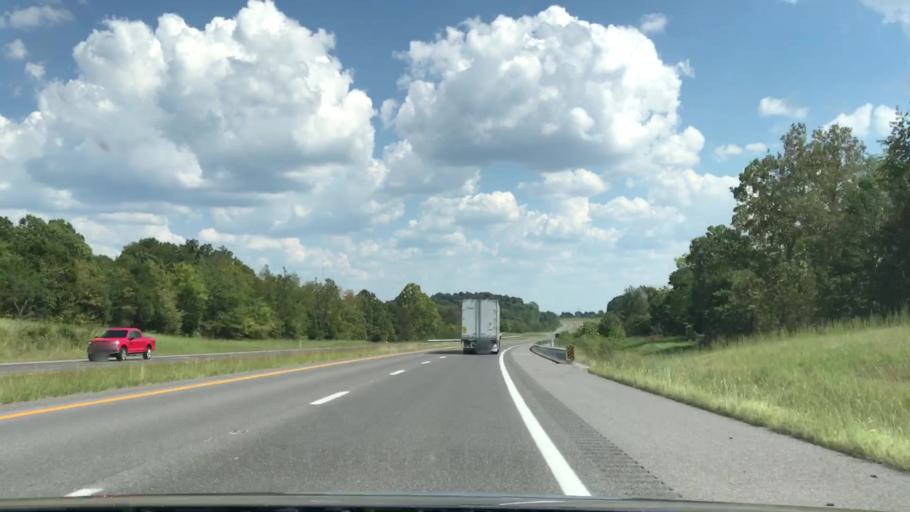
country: US
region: Kentucky
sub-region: Caldwell County
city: Princeton
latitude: 37.1107
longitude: -87.9640
